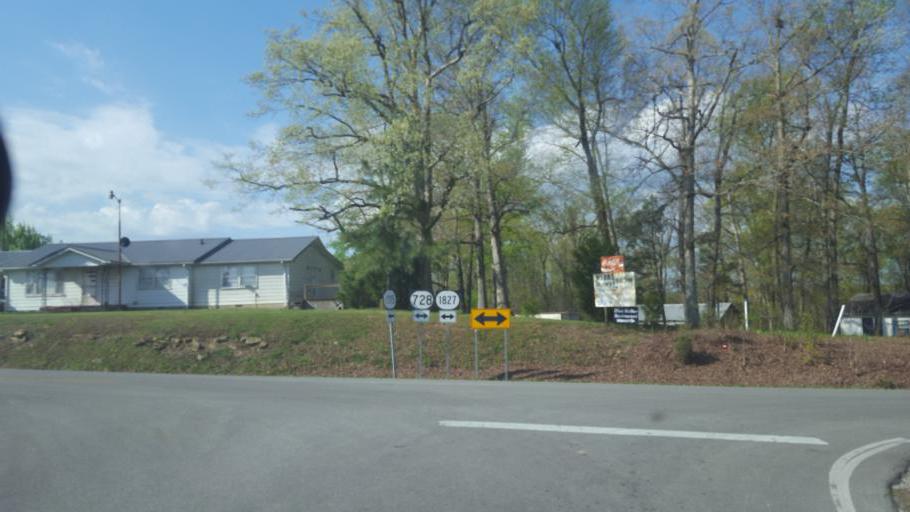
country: US
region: Kentucky
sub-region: Edmonson County
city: Brownsville
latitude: 37.2693
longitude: -86.1605
